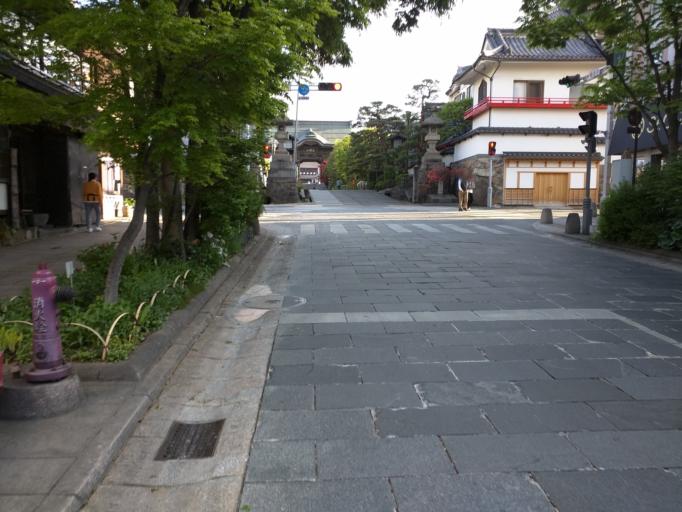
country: JP
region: Nagano
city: Nagano-shi
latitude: 36.6572
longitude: 138.1875
